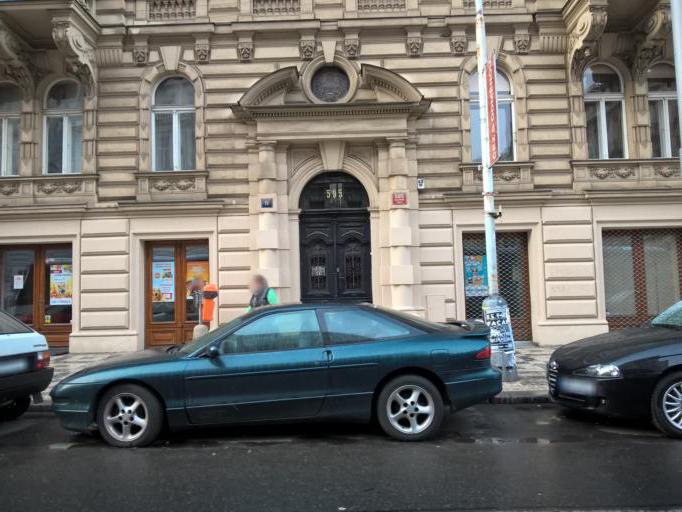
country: CZ
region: Praha
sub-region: Praha 1
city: Mala Strana
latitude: 50.0804
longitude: 14.4046
